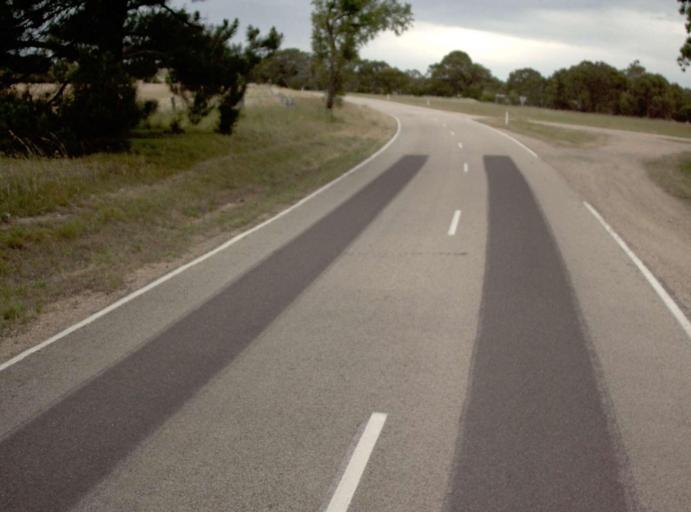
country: AU
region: Victoria
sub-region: East Gippsland
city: Bairnsdale
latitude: -37.9726
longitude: 147.4673
